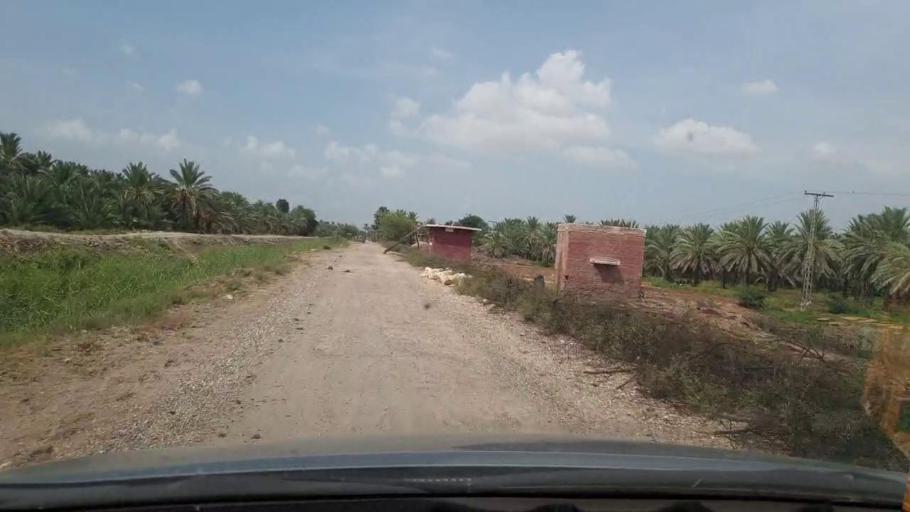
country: PK
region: Sindh
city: Khairpur
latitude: 27.5167
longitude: 68.8816
